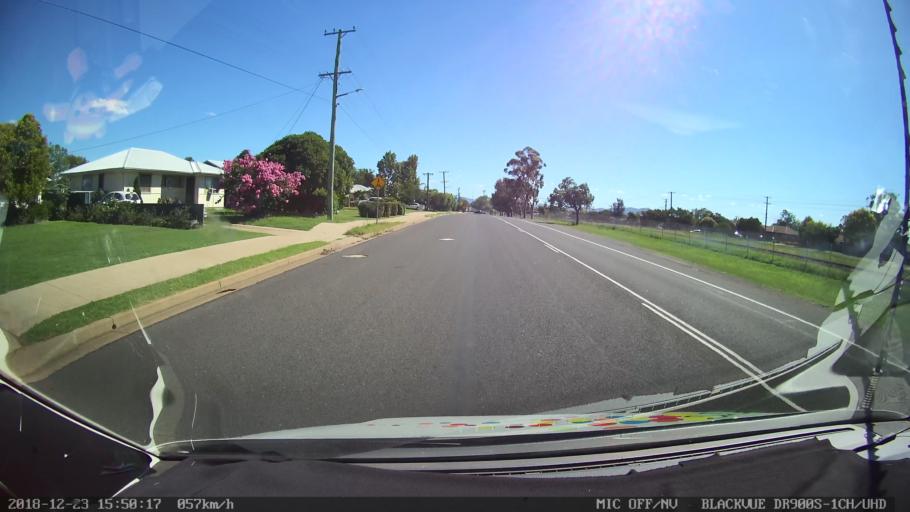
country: AU
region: New South Wales
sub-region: Tamworth Municipality
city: South Tamworth
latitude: -31.1052
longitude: 150.9015
